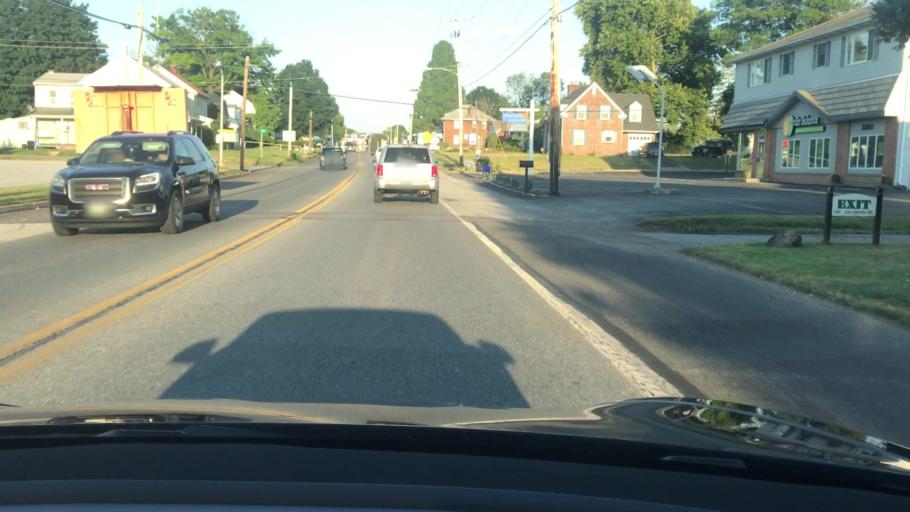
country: US
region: Pennsylvania
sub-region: York County
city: Shiloh
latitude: 39.9788
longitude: -76.8001
